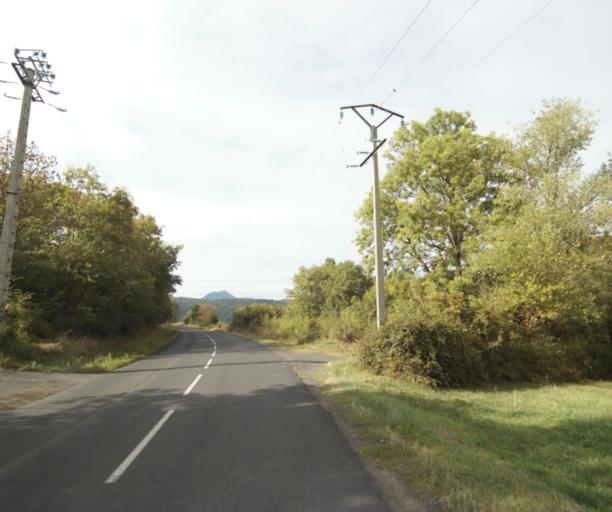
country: FR
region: Auvergne
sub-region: Departement du Puy-de-Dome
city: Romagnat
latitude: 45.7127
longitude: 3.0863
